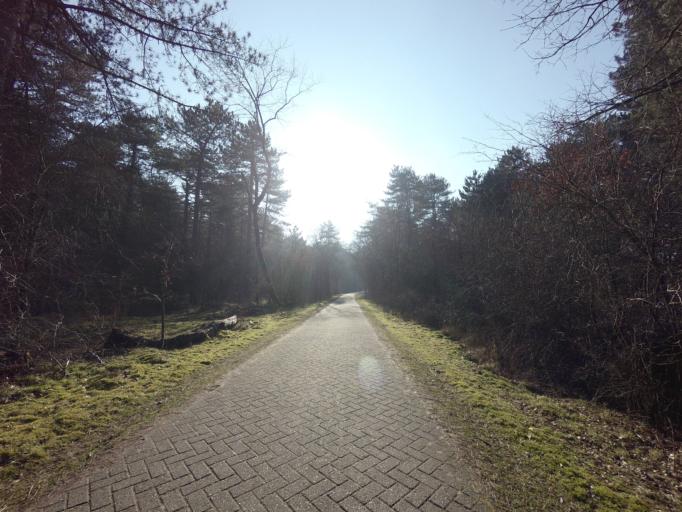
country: NL
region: North Holland
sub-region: Gemeente Bloemendaal
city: Bloemendaal
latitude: 52.4165
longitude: 4.6076
